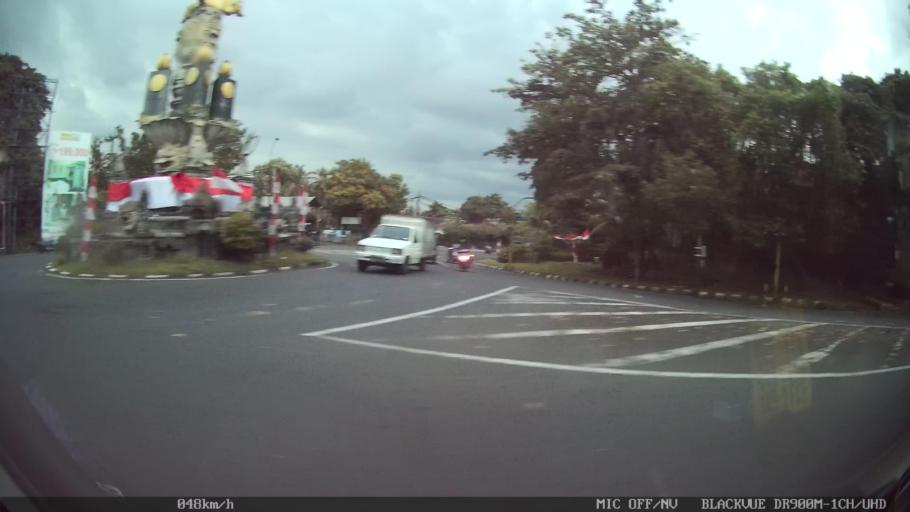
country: ID
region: Bali
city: Banjar Penyalin
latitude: -8.5370
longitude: 115.1111
